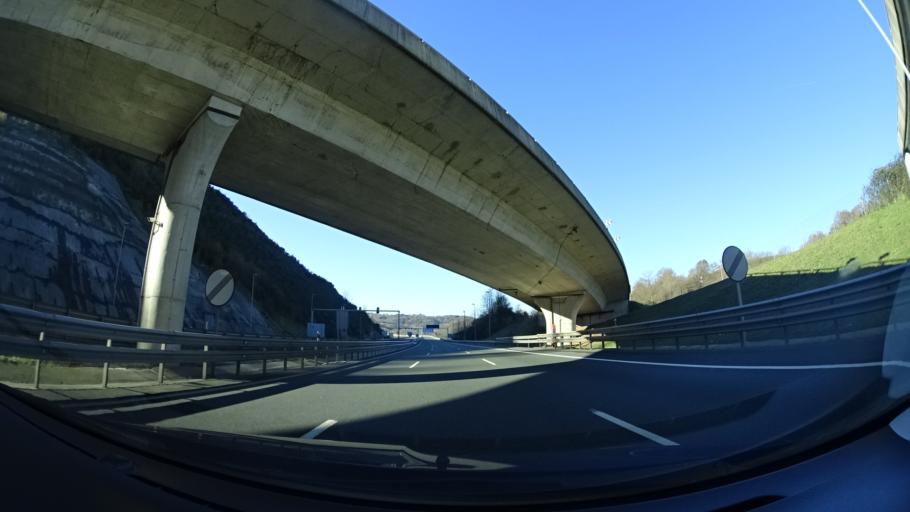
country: ES
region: Basque Country
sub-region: Provincia de Guipuzcoa
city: Astigarraga
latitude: 43.2898
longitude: -1.9400
